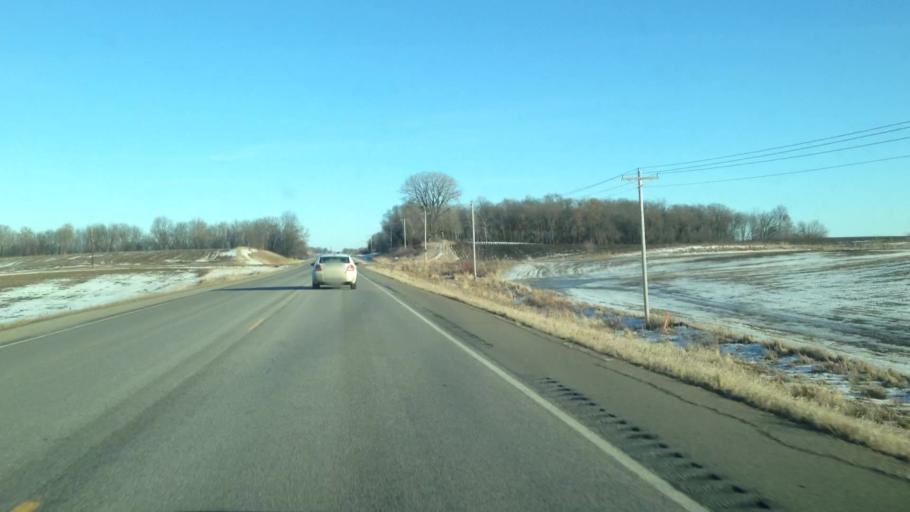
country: US
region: Minnesota
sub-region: Rice County
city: Lonsdale
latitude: 44.5437
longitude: -93.4708
